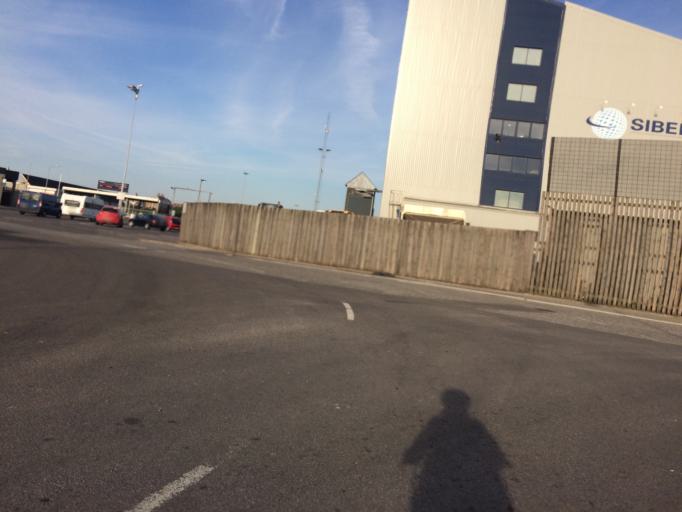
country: DK
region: Capital Region
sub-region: Bornholm Kommune
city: Ronne
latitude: 55.1005
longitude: 14.6868
